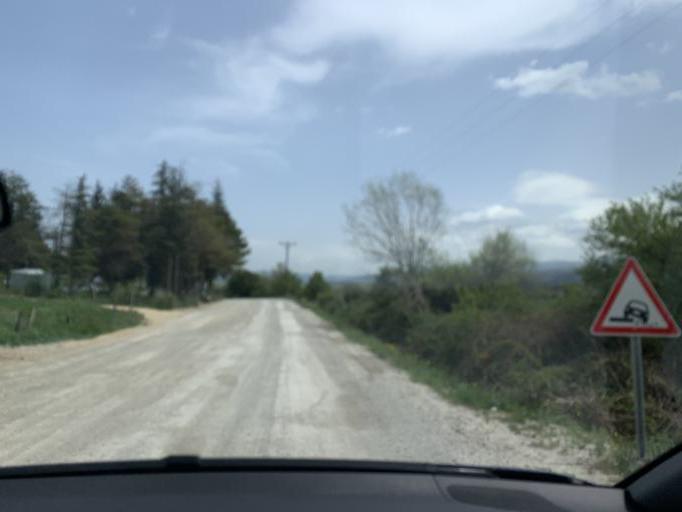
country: TR
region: Bolu
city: Bolu
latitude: 40.7604
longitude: 31.6994
